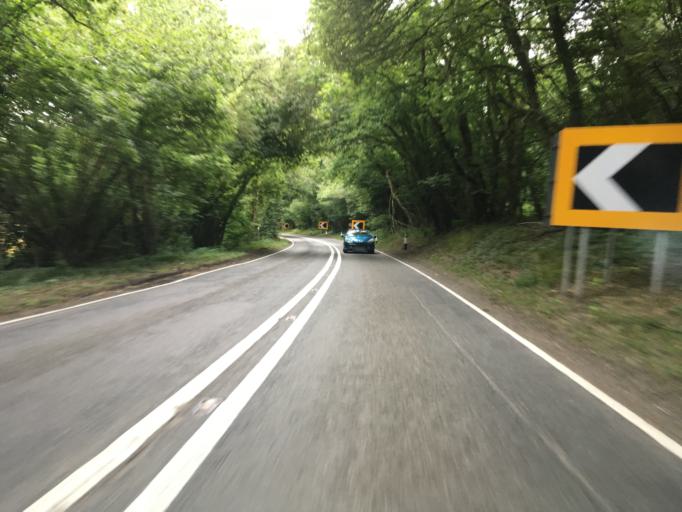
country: GB
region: England
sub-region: Hampshire
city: Four Marks
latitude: 51.0209
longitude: -1.0248
